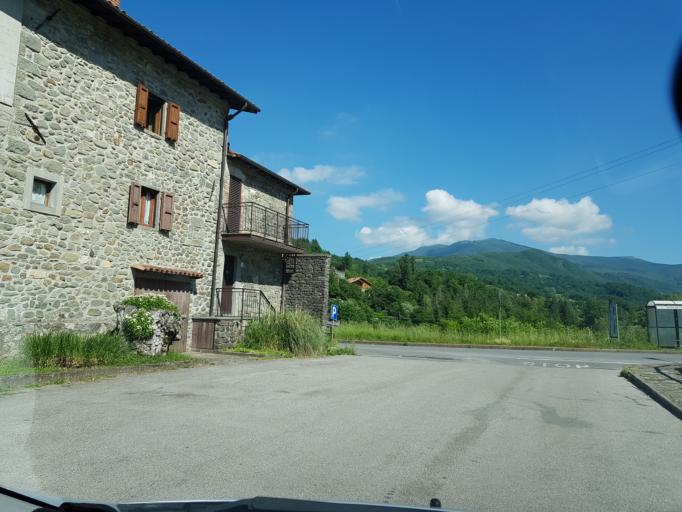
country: IT
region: Tuscany
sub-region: Provincia di Lucca
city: Piazza al Serchio-San Michele
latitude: 44.1832
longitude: 10.3030
